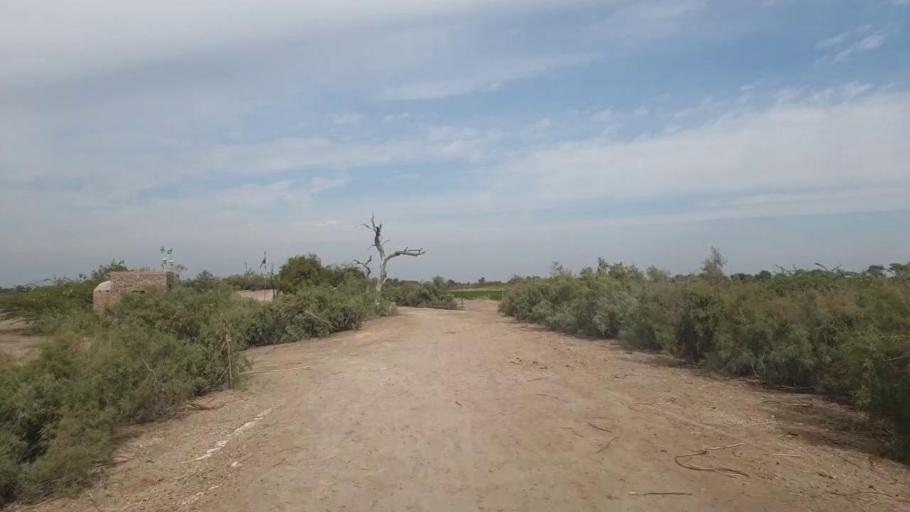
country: PK
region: Sindh
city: Sanghar
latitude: 26.0552
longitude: 68.9087
